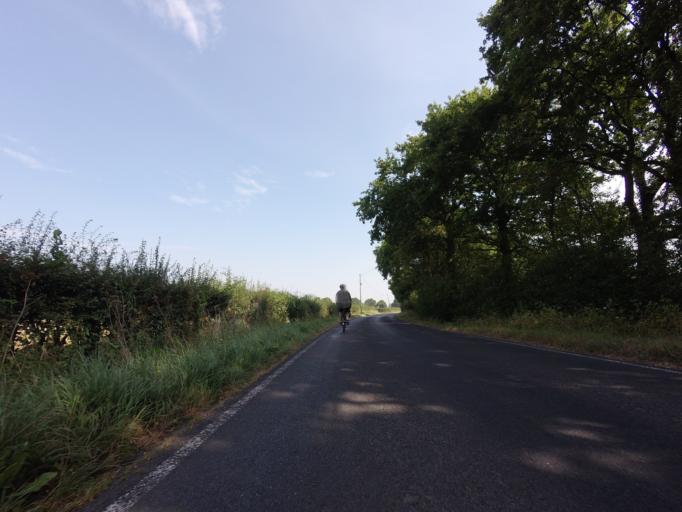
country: GB
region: England
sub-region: Kent
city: Headcorn
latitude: 51.1477
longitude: 0.5945
